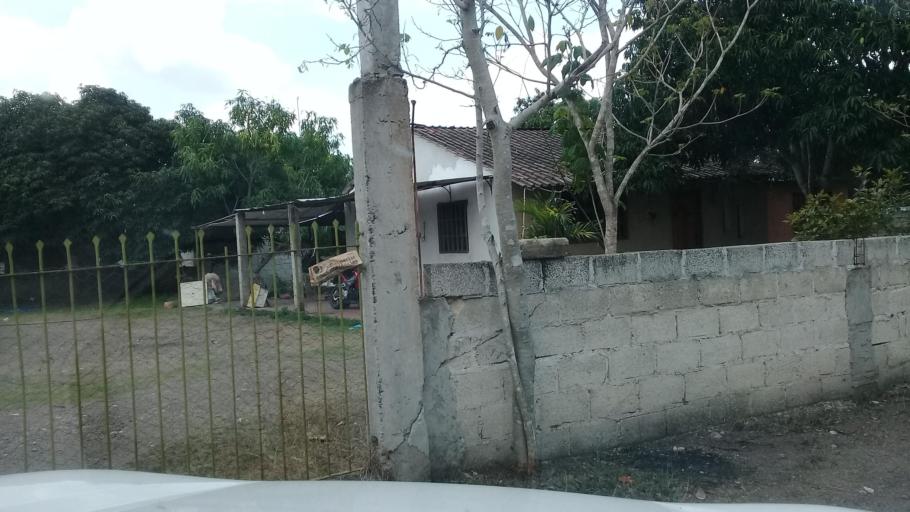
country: MX
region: Veracruz
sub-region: Emiliano Zapata
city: Plan del Rio
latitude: 19.3544
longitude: -96.6440
